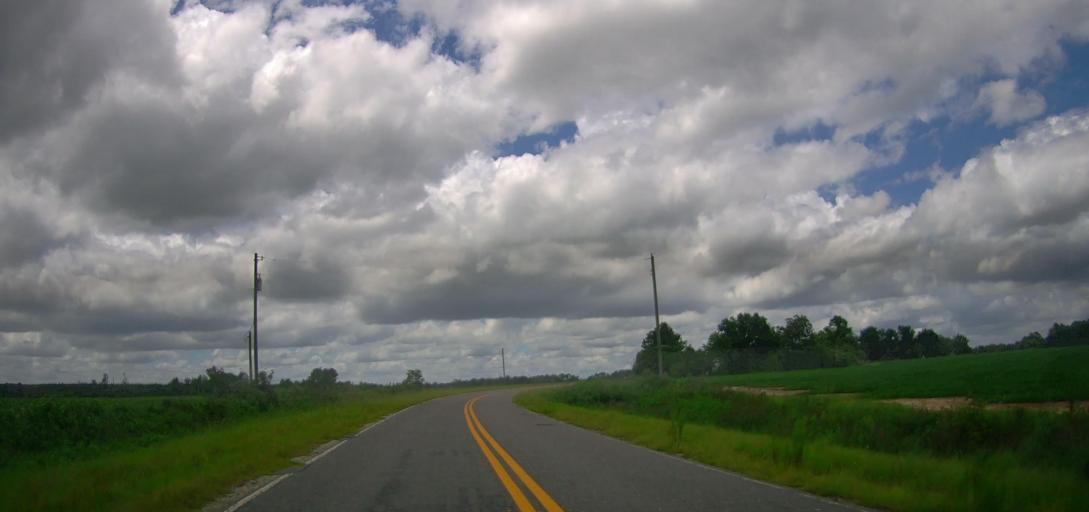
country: US
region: Georgia
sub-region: Irwin County
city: Ocilla
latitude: 31.6490
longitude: -83.3998
